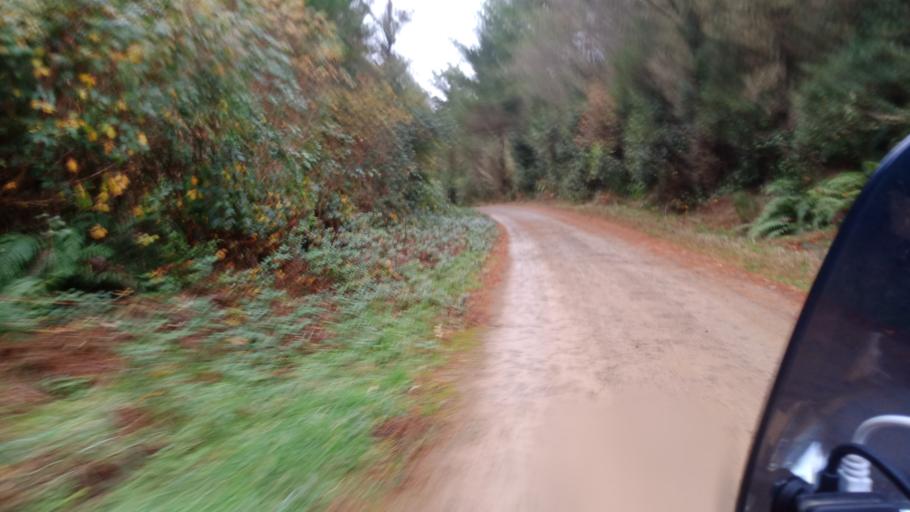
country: NZ
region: Bay of Plenty
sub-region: Whakatane District
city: Murupara
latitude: -38.6655
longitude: 176.6312
